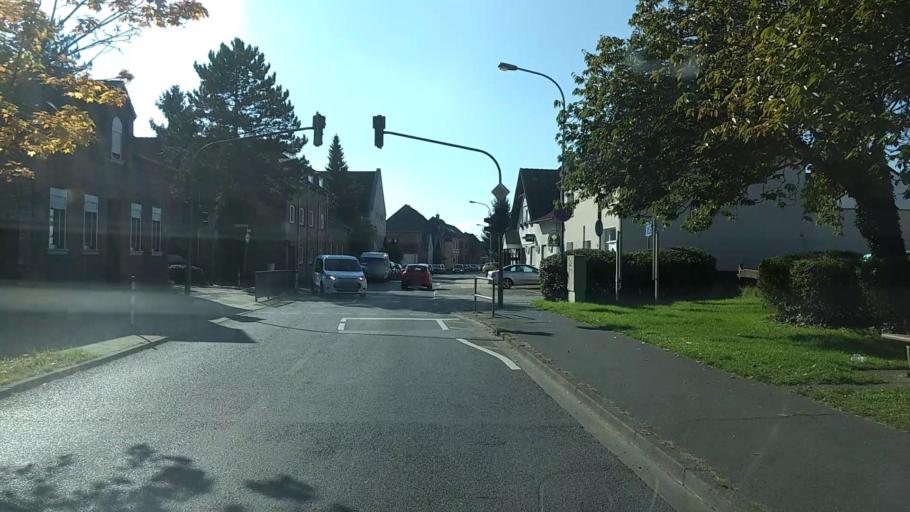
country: DE
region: North Rhine-Westphalia
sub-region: Regierungsbezirk Koln
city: Kerpen
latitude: 50.9100
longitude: 6.6784
